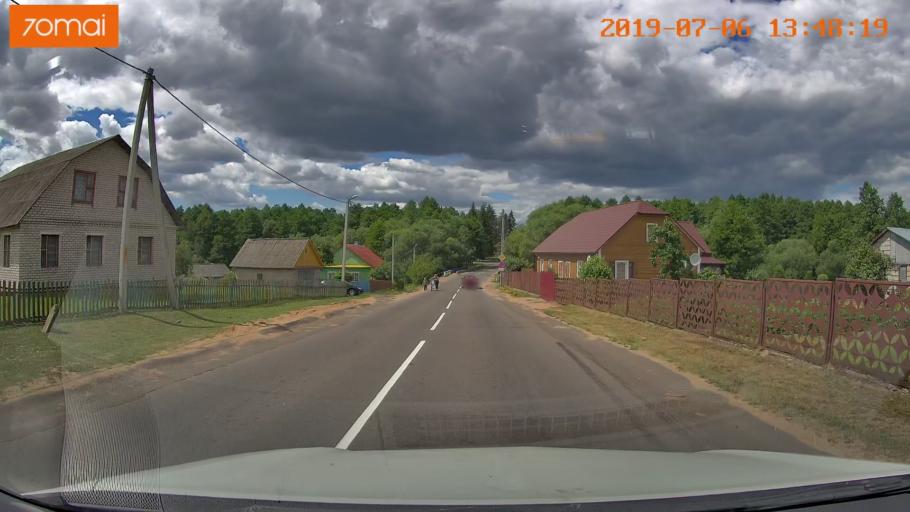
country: BY
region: Minsk
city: Enyerhyetykaw
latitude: 53.6895
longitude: 26.8588
